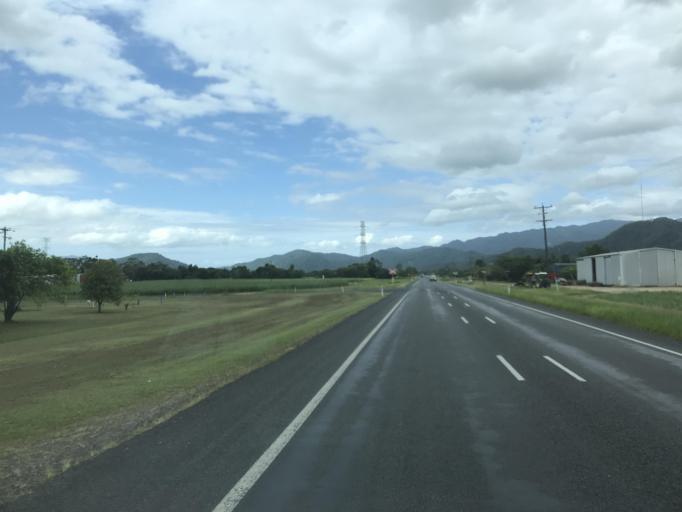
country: AU
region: Queensland
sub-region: Cassowary Coast
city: Innisfail
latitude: -17.7861
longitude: 146.0224
